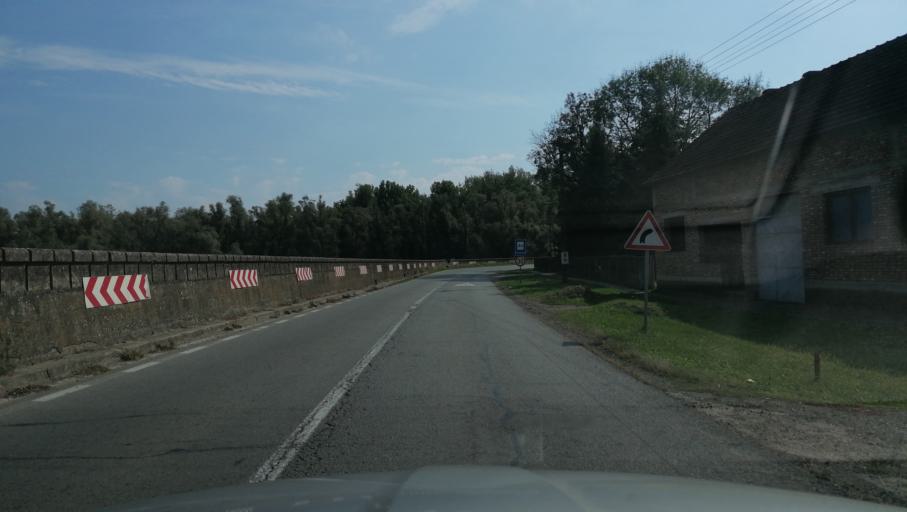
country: RS
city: Bosut
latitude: 44.9396
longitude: 19.3688
